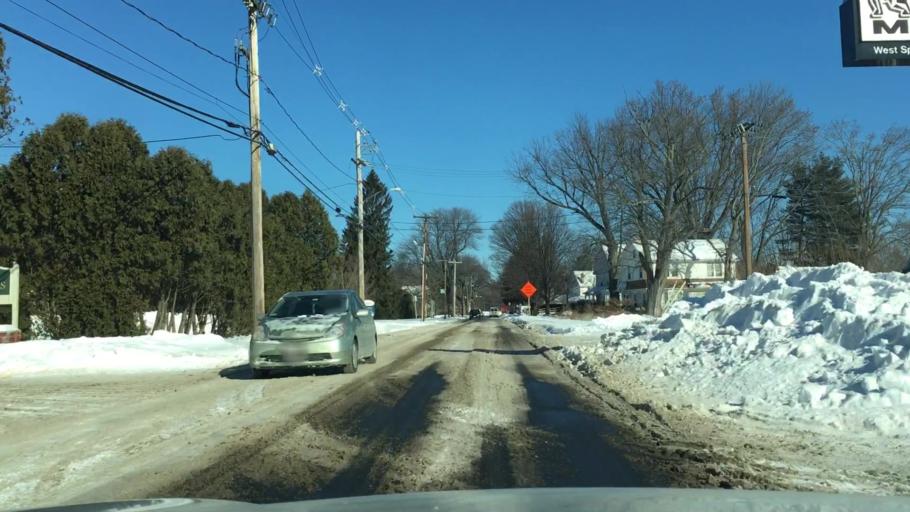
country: US
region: Massachusetts
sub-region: Hampden County
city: Chicopee
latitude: 42.1399
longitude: -72.6234
